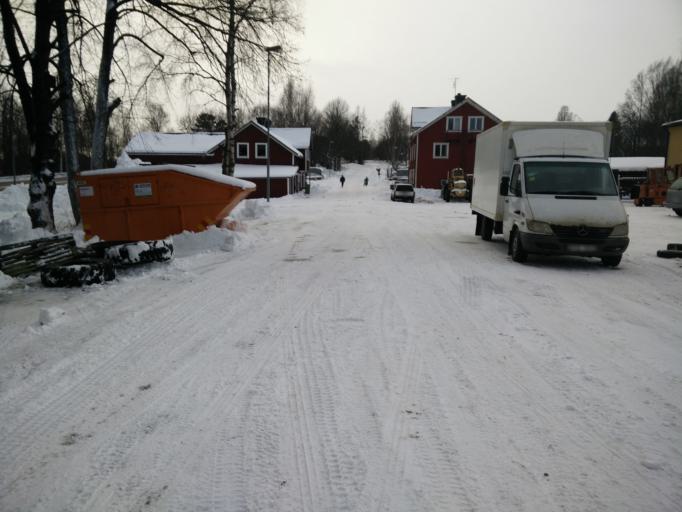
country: SE
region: Vaesternorrland
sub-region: Sundsvalls Kommun
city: Kvissleby
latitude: 62.2921
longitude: 17.3778
